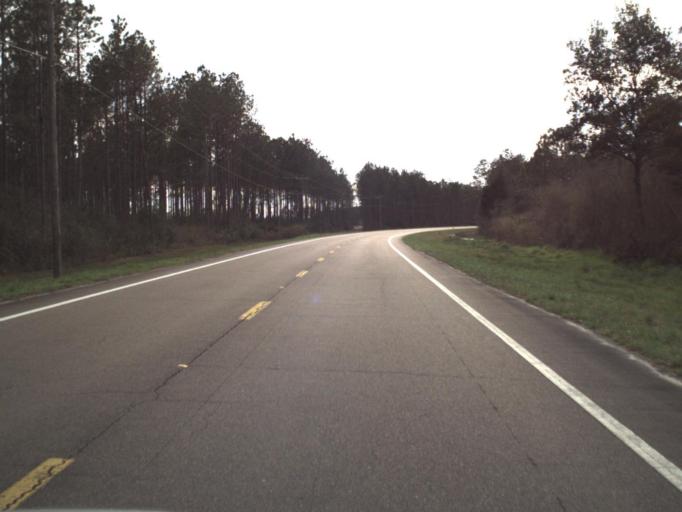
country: US
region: Florida
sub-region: Gulf County
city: Wewahitchka
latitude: 30.1348
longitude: -85.3408
